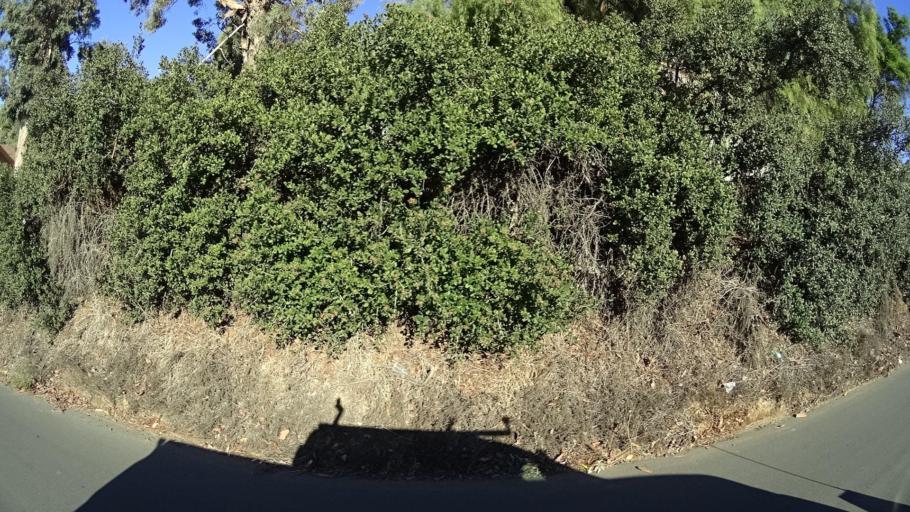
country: US
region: California
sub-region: San Diego County
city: Bonita
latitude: 32.6768
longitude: -117.0217
